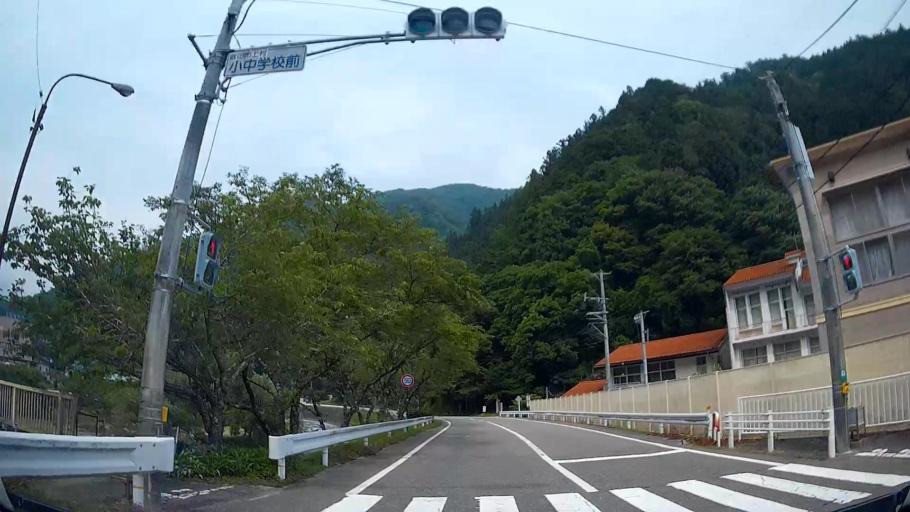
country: JP
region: Nagano
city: Iida
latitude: 35.3844
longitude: 137.9687
